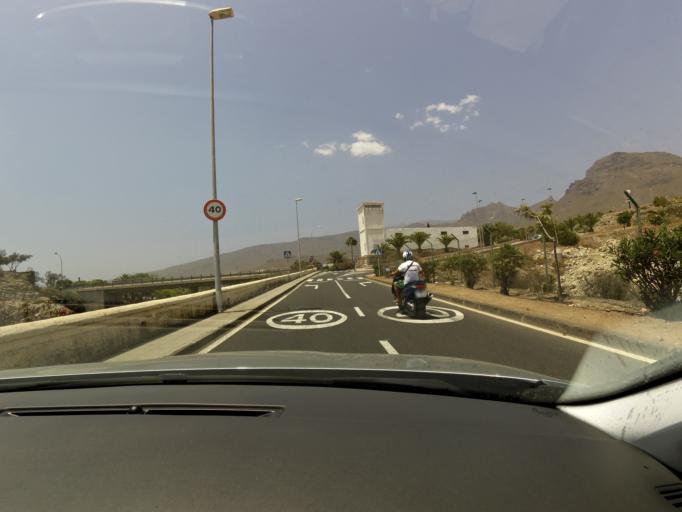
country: ES
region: Canary Islands
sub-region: Provincia de Santa Cruz de Tenerife
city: Playa de las Americas
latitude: 28.0855
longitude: -16.7286
